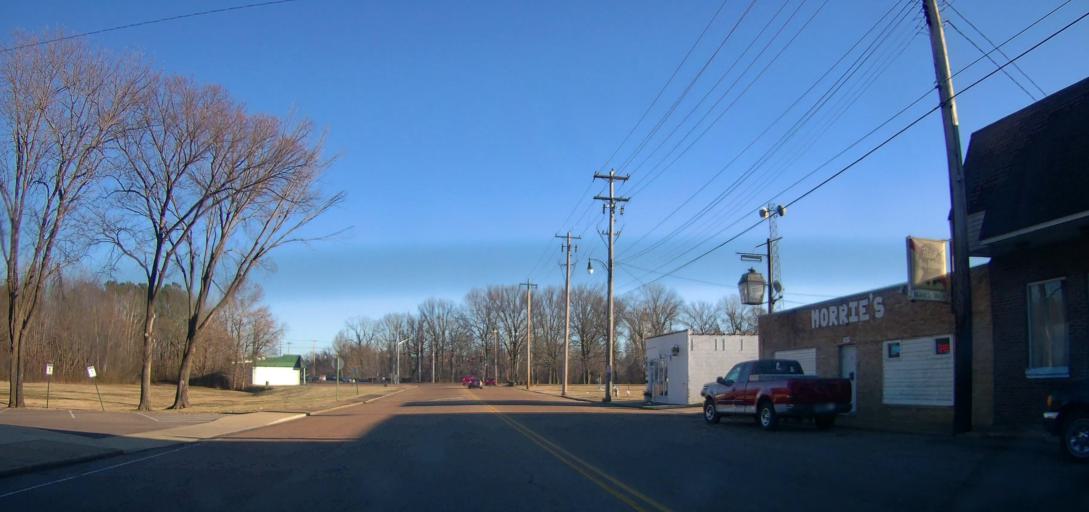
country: US
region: Tennessee
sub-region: Shelby County
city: Millington
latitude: 35.3421
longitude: -89.8918
